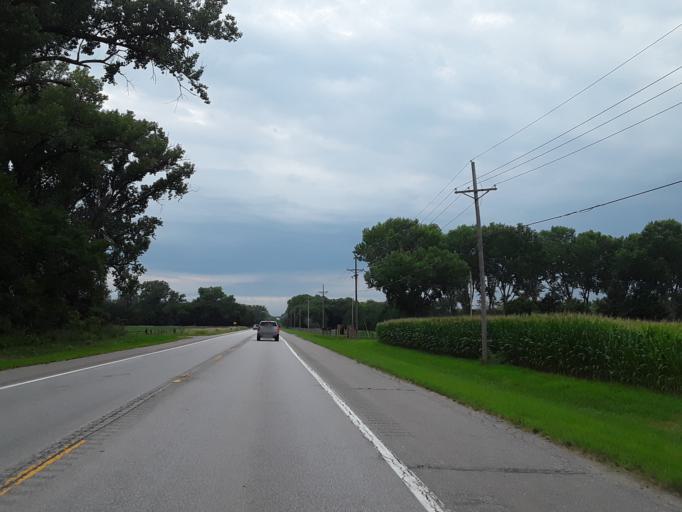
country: US
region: Nebraska
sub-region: Saunders County
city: Yutan
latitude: 41.2338
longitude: -96.3432
